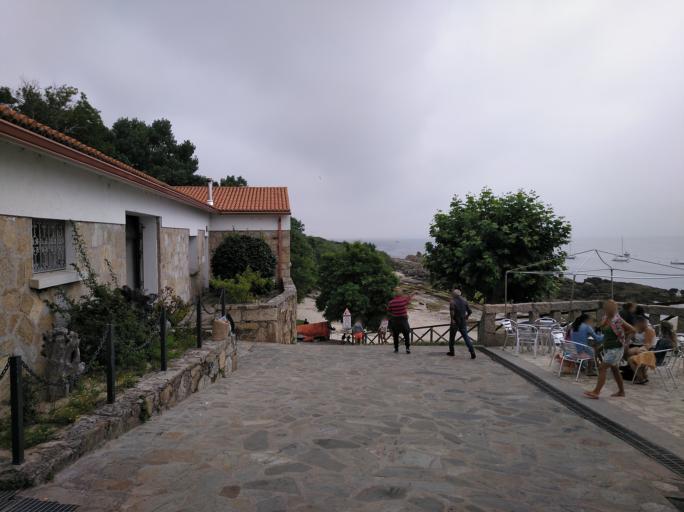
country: ES
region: Galicia
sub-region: Provincia de Pontevedra
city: Sanxenxo
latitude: 42.3767
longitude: -8.9320
